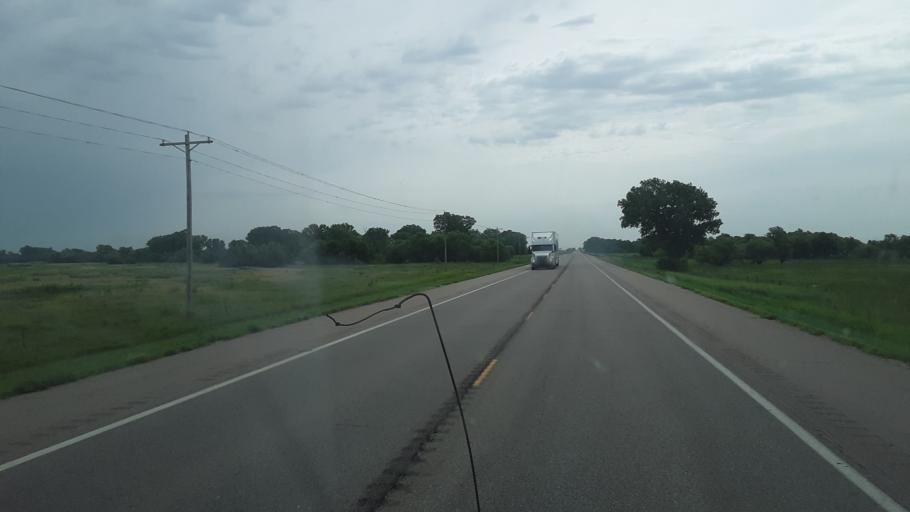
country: US
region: Kansas
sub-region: Stafford County
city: Saint John
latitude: 37.9559
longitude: -98.8269
